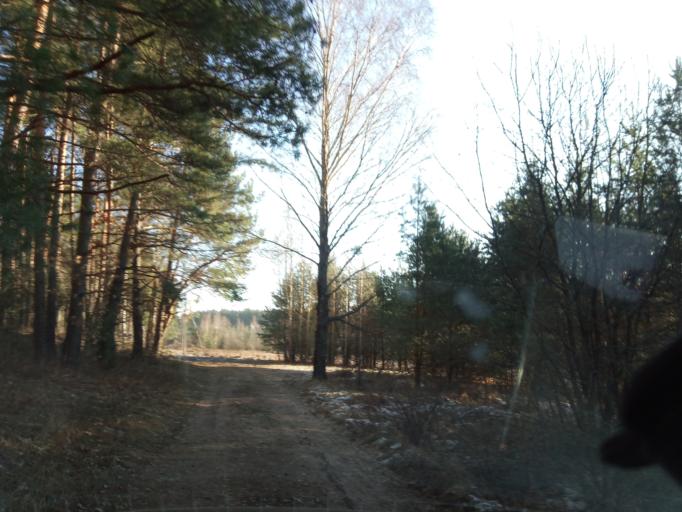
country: LT
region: Alytaus apskritis
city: Druskininkai
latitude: 53.9496
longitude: 23.8737
